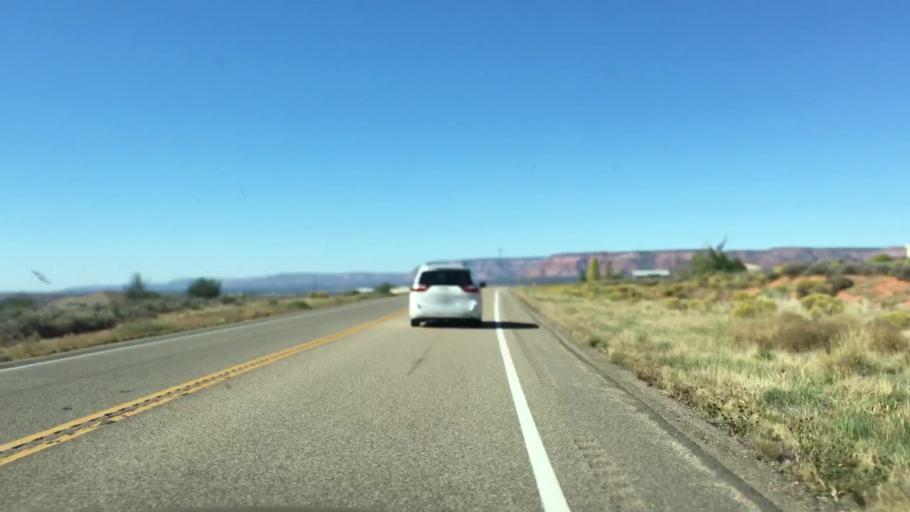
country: US
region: Utah
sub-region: Kane County
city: Kanab
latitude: 37.0233
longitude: -112.4350
